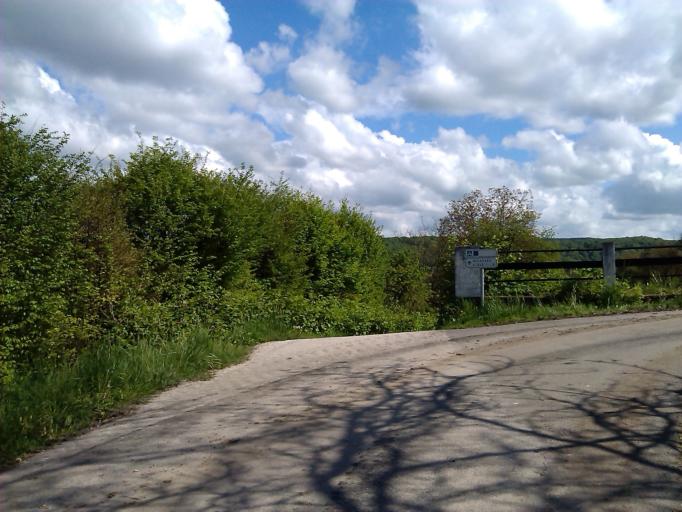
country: FR
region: Franche-Comte
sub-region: Departement du Doubs
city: Colombier-Fontaine
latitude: 47.4383
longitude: 6.6288
